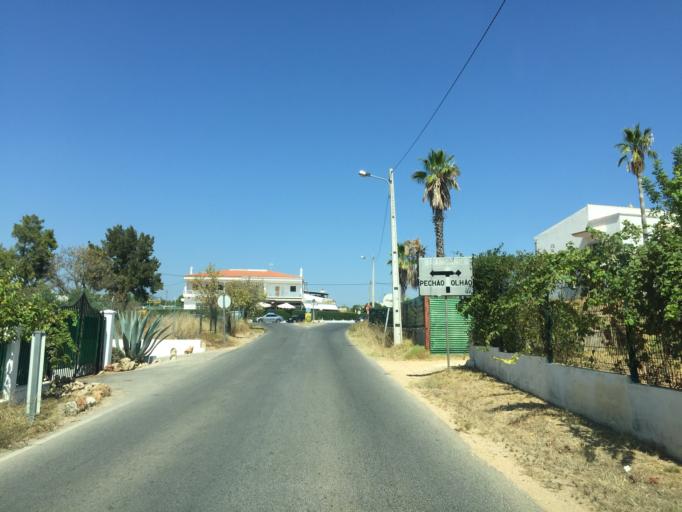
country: PT
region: Faro
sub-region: Olhao
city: Olhao
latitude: 37.0490
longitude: -7.8672
